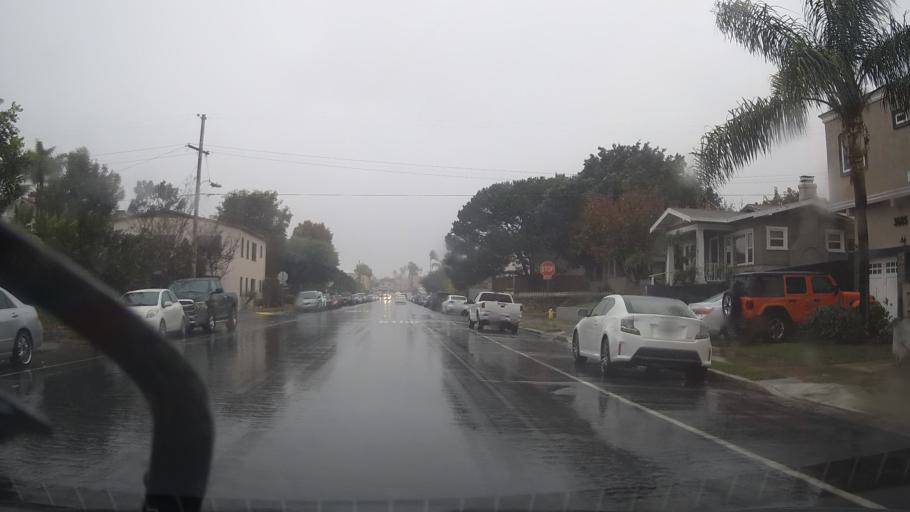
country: US
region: California
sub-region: San Diego County
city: San Diego
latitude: 32.7453
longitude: -117.1368
